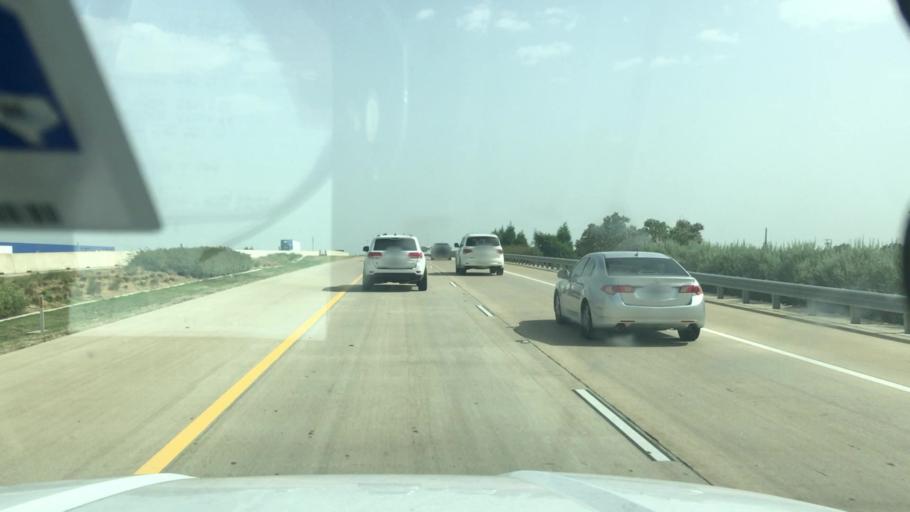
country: US
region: Texas
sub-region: Dallas County
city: Grand Prairie
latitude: 32.6933
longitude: -97.0246
